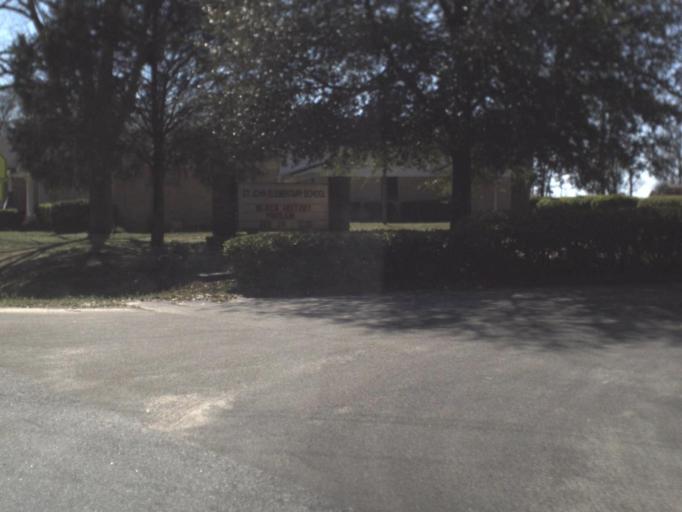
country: US
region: Florida
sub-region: Gadsden County
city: Gretna
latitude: 30.6592
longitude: -84.6060
